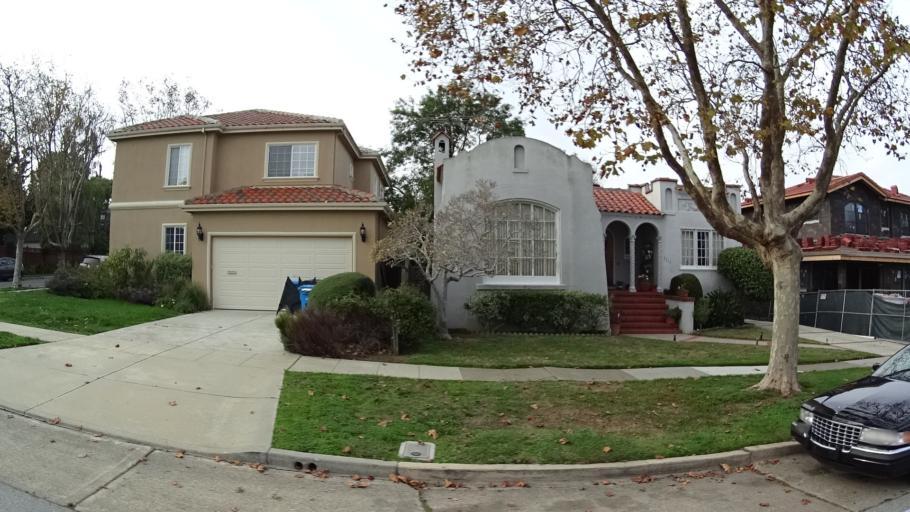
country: US
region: California
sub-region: San Mateo County
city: Hillsborough
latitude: 37.5816
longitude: -122.3772
